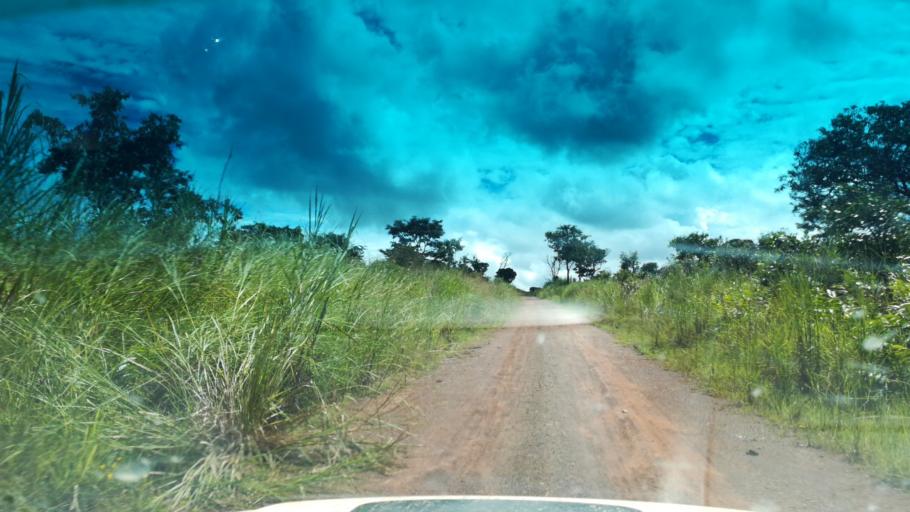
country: ZM
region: Northern
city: Kaputa
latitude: -7.7710
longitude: 29.2256
